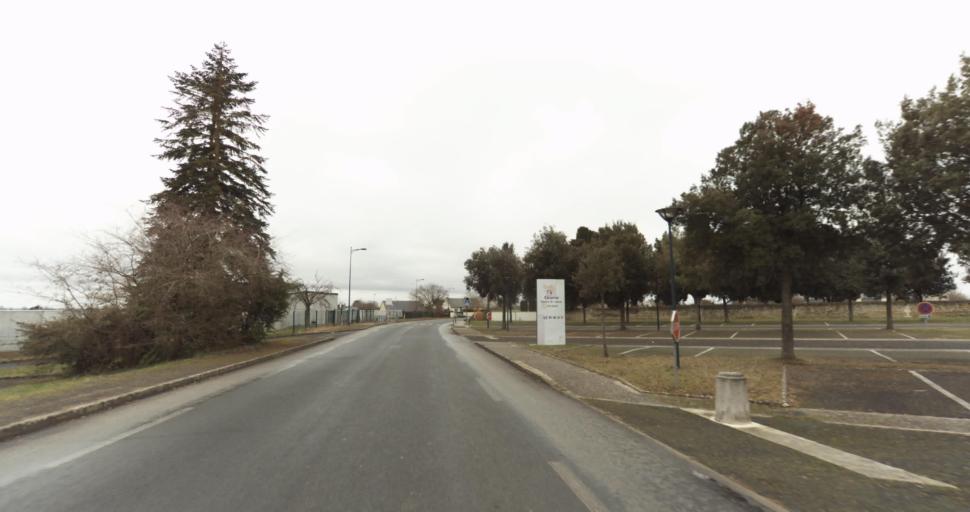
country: FR
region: Pays de la Loire
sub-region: Departement de Maine-et-Loire
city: Montreuil-Bellay
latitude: 47.1307
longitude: -0.1474
